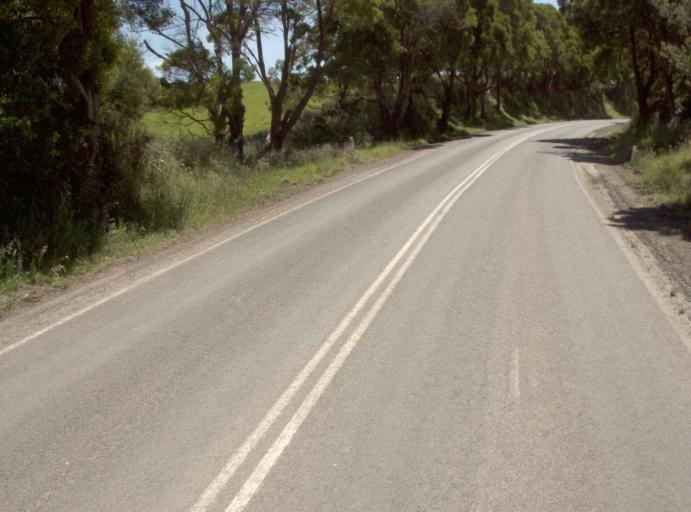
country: AU
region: Victoria
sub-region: Bass Coast
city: North Wonthaggi
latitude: -38.6957
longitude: 146.0945
